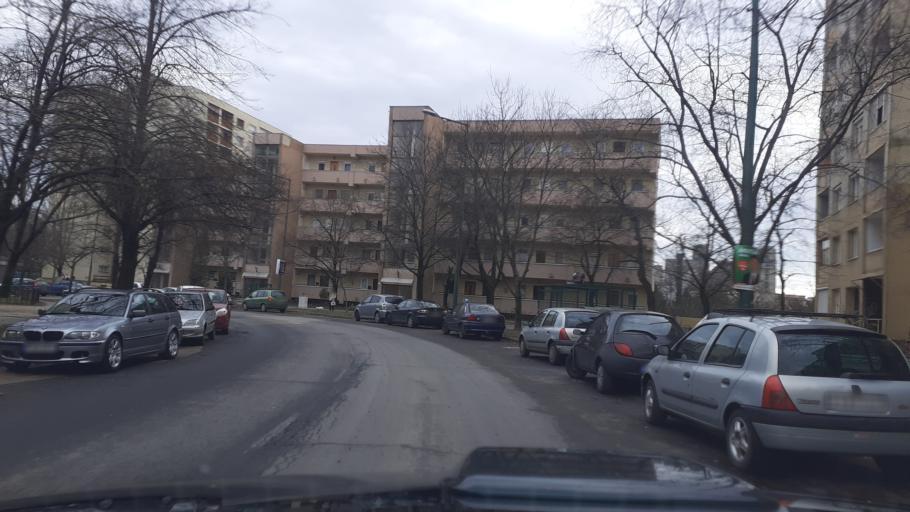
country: HU
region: Fejer
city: dunaujvaros
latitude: 46.9704
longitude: 18.9332
